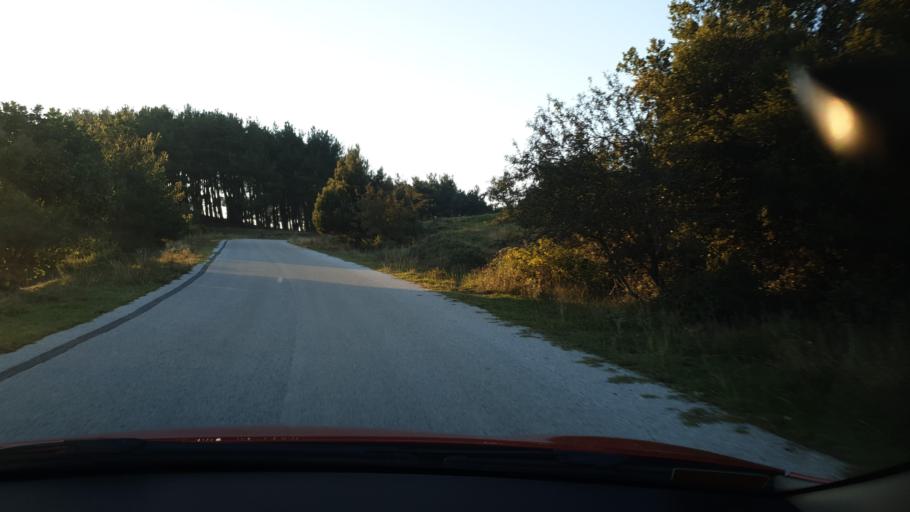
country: GR
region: Central Macedonia
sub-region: Nomos Thessalonikis
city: Peristera
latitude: 40.5100
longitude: 23.2205
